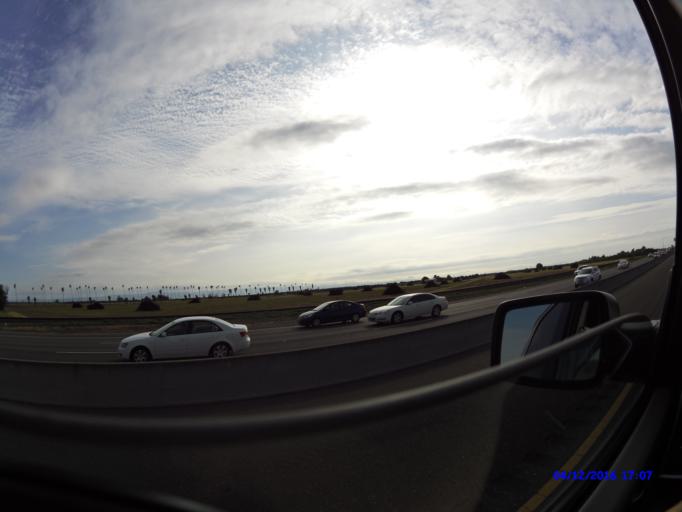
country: US
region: California
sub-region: San Joaquin County
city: Ripon
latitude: 37.7681
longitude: -121.1696
